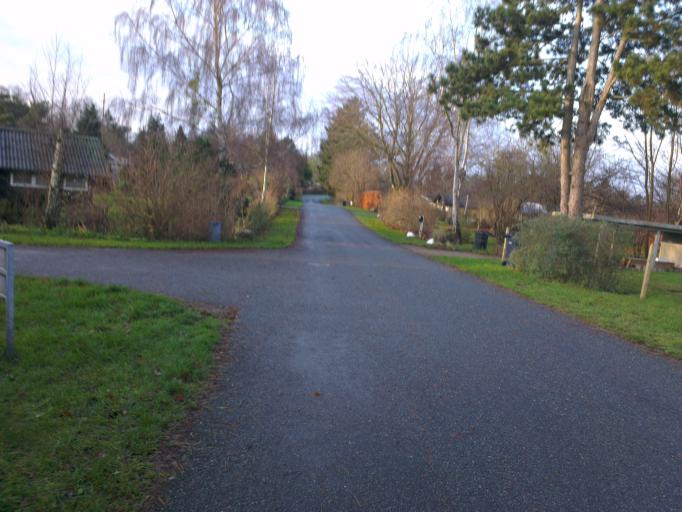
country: DK
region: Capital Region
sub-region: Frederikssund Kommune
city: Jaegerspris
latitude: 55.8396
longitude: 11.9678
